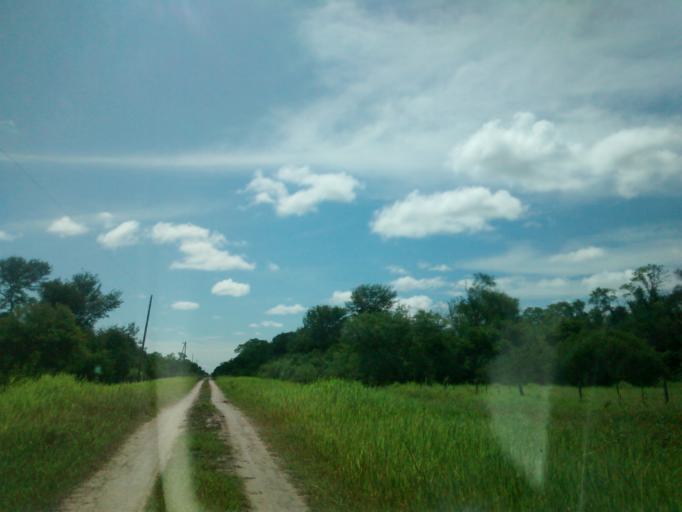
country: AR
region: Chaco
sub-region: Departamento de Quitilipi
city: Quitilipi
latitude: -26.7667
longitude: -60.2707
